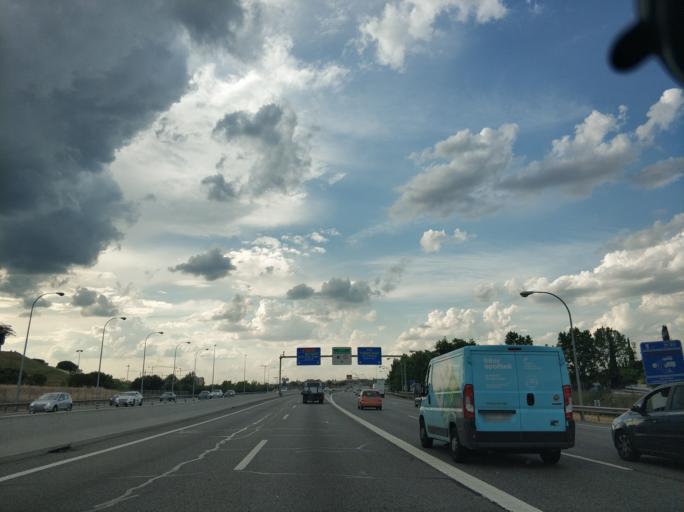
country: ES
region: Madrid
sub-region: Provincia de Madrid
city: Usera
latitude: 40.3766
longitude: -3.6838
